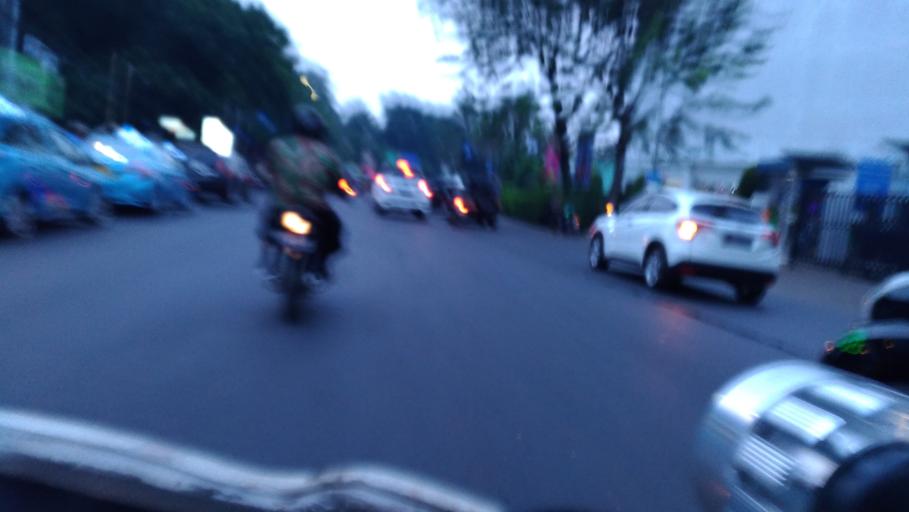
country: ID
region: West Java
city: Cileungsir
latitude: -6.3696
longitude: 106.8934
